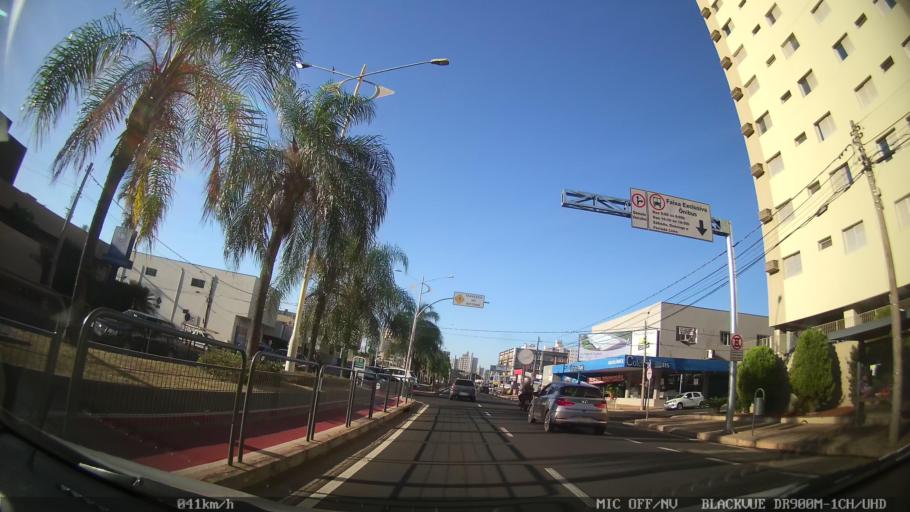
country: BR
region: Sao Paulo
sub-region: Sao Jose Do Rio Preto
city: Sao Jose do Rio Preto
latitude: -20.8144
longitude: -49.3910
